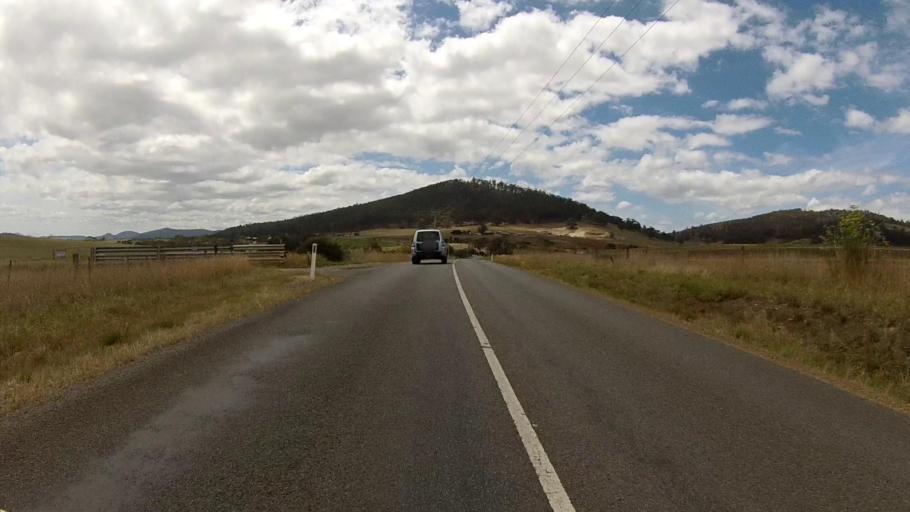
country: AU
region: Tasmania
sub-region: Sorell
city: Sorell
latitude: -42.8049
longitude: 147.6132
